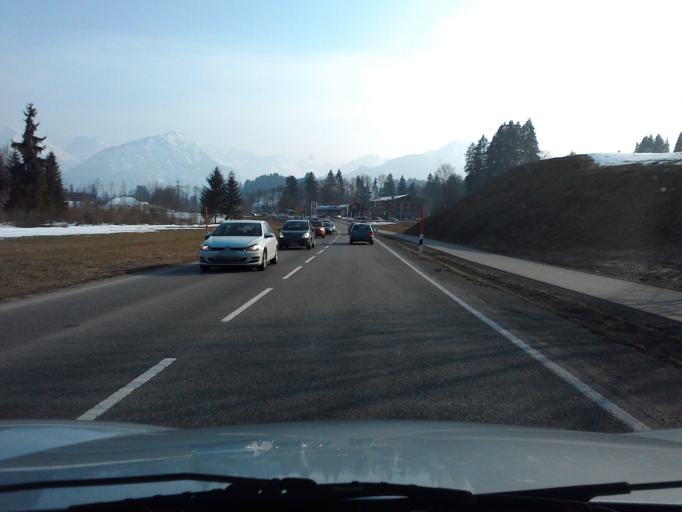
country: DE
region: Bavaria
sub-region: Swabia
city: Oberstdorf
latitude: 47.4285
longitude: 10.2670
